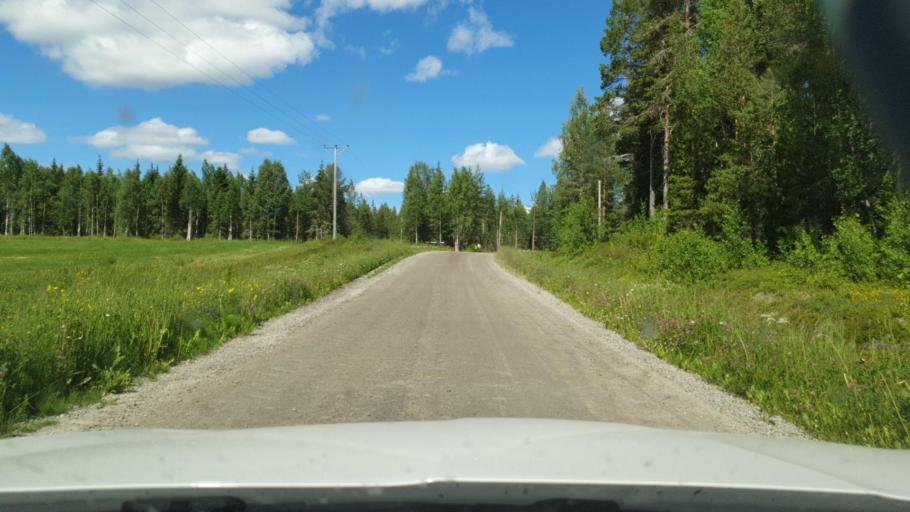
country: SE
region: Vaesterbotten
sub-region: Skelleftea Kommun
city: Backa
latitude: 65.1524
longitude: 21.1613
